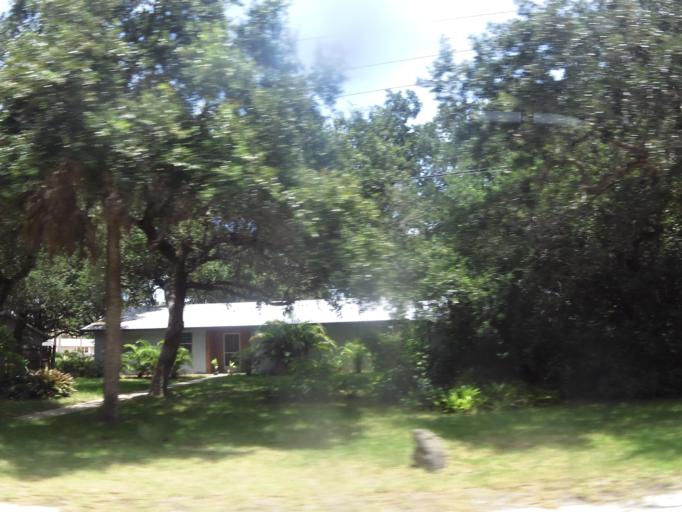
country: US
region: Florida
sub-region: Volusia County
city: Ponce Inlet
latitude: 29.0850
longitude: -80.9323
